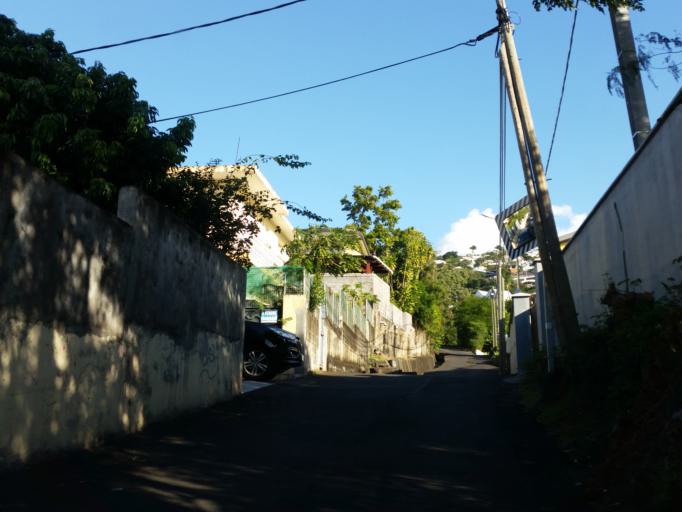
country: RE
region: Reunion
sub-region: Reunion
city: Saint-Denis
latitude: -20.8973
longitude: 55.4582
